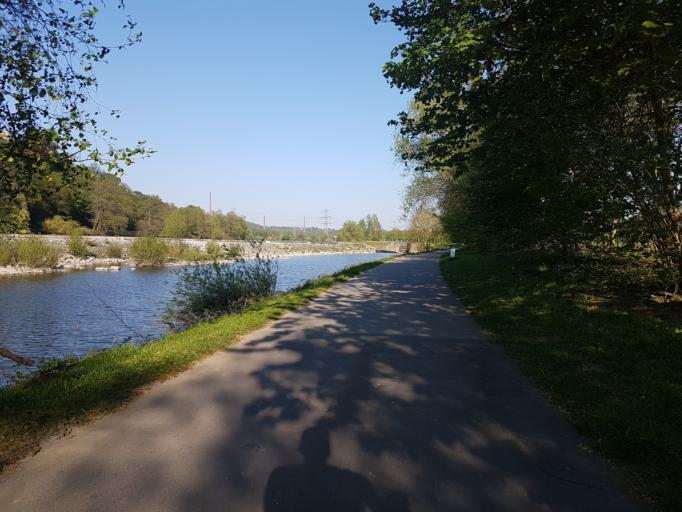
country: DE
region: North Rhine-Westphalia
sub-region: Regierungsbezirk Munster
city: Gelsenkirchen
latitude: 51.4287
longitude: 7.1093
